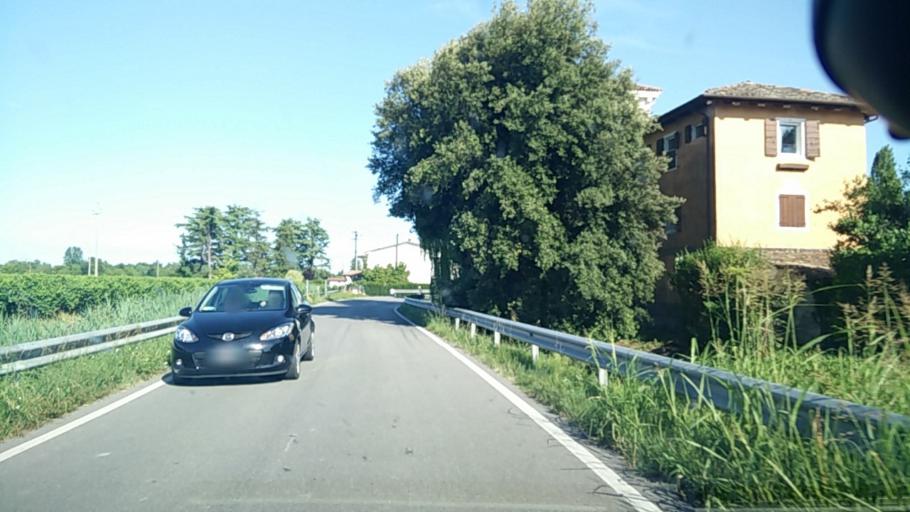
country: IT
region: Veneto
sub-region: Provincia di Treviso
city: San Biagio di Callalta
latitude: 45.6846
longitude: 12.3937
